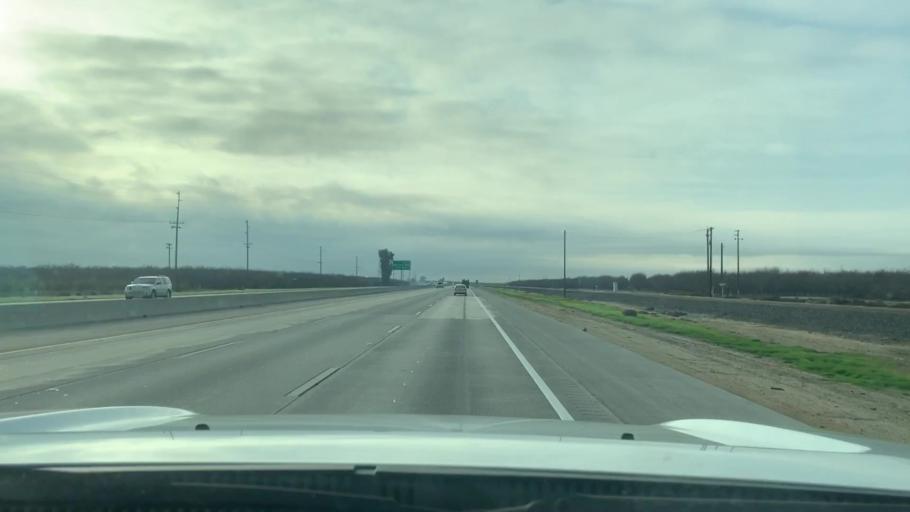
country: US
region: California
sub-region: Kern County
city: Shafter
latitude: 35.5454
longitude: -119.1952
